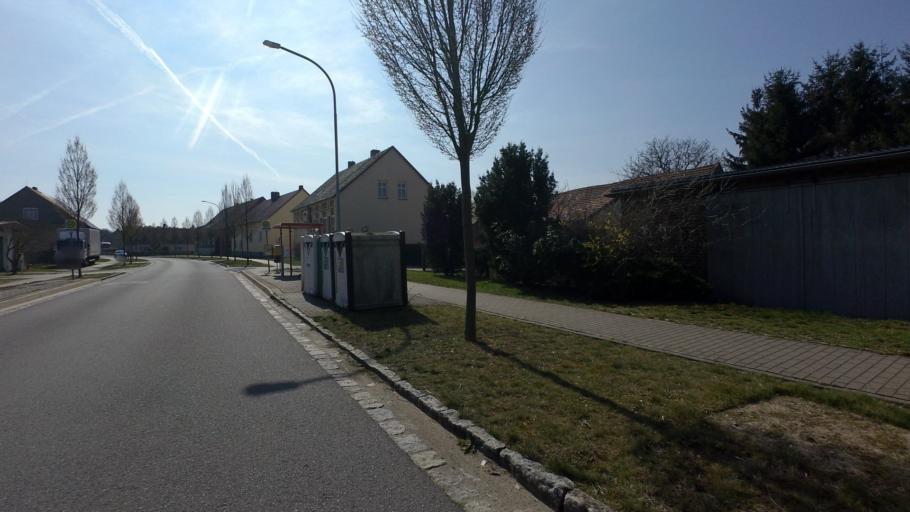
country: DE
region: Brandenburg
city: Golssen
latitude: 51.9608
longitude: 13.5889
